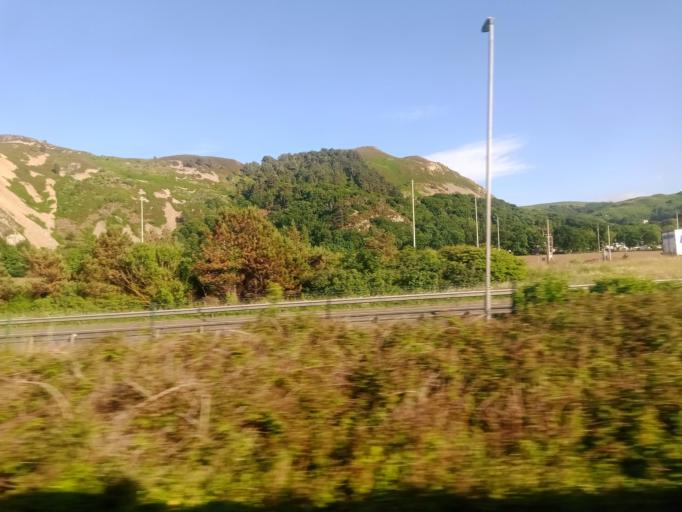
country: GB
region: Wales
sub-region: Conwy
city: Conwy
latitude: 53.2850
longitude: -3.8917
